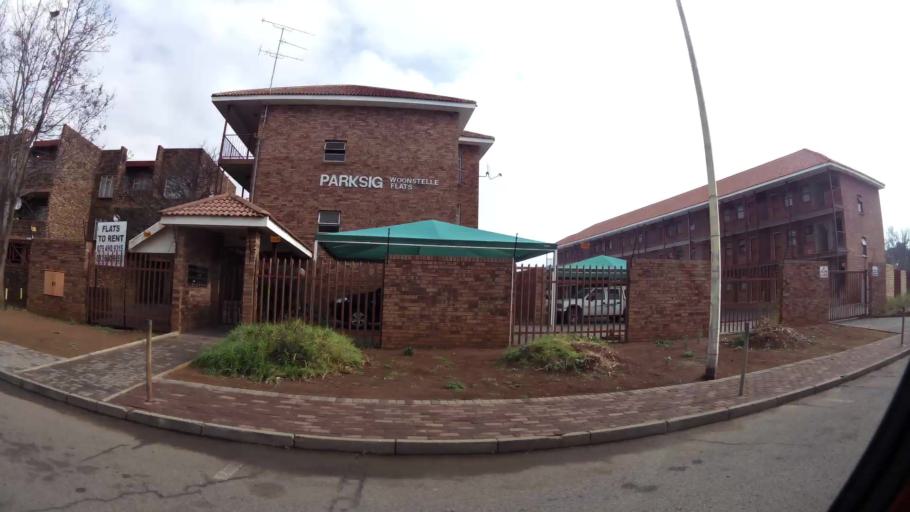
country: ZA
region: Gauteng
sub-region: Sedibeng District Municipality
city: Vanderbijlpark
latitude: -26.6959
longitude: 27.8341
